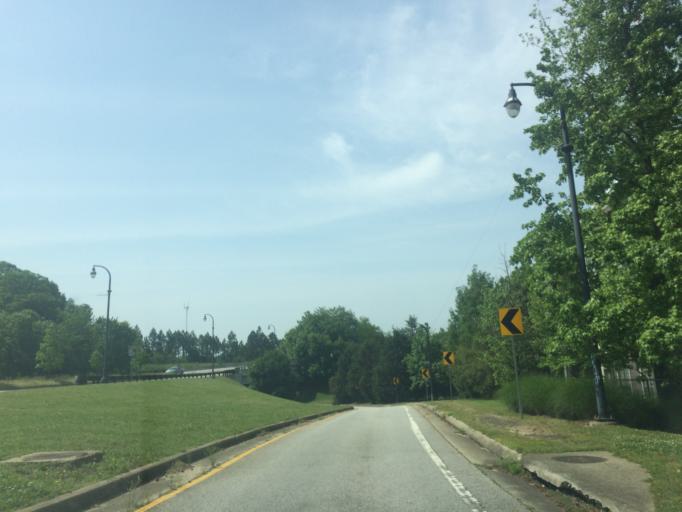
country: US
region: Georgia
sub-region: DeKalb County
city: Druid Hills
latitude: 33.7667
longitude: -84.3587
